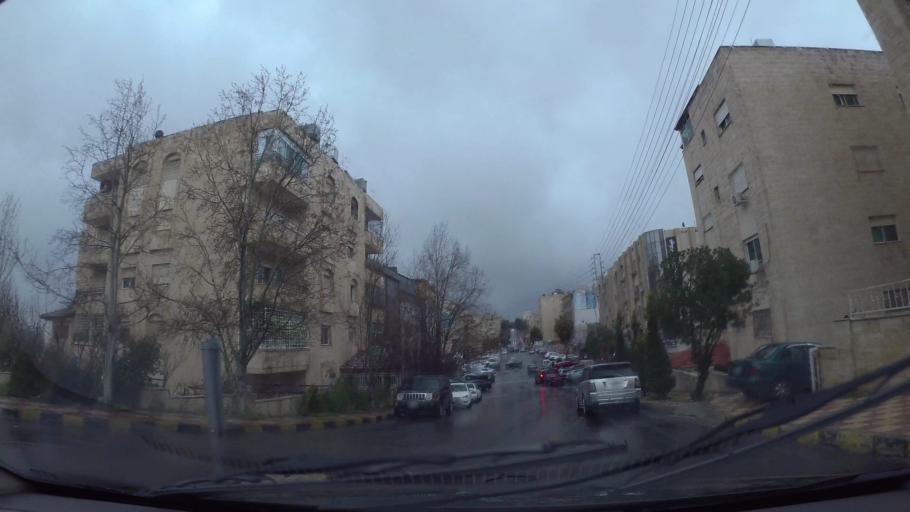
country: JO
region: Amman
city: Al Jubayhah
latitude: 32.0176
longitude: 35.8806
